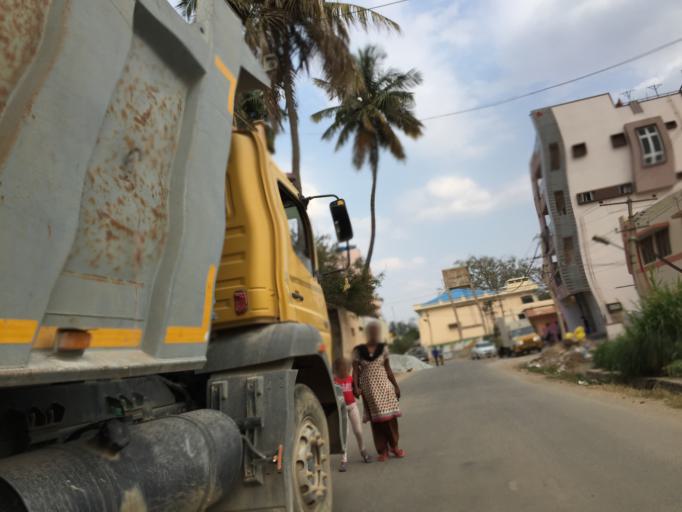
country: IN
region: Karnataka
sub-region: Chikkaballapur
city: Chik Ballapur
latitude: 13.4281
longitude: 77.7287
